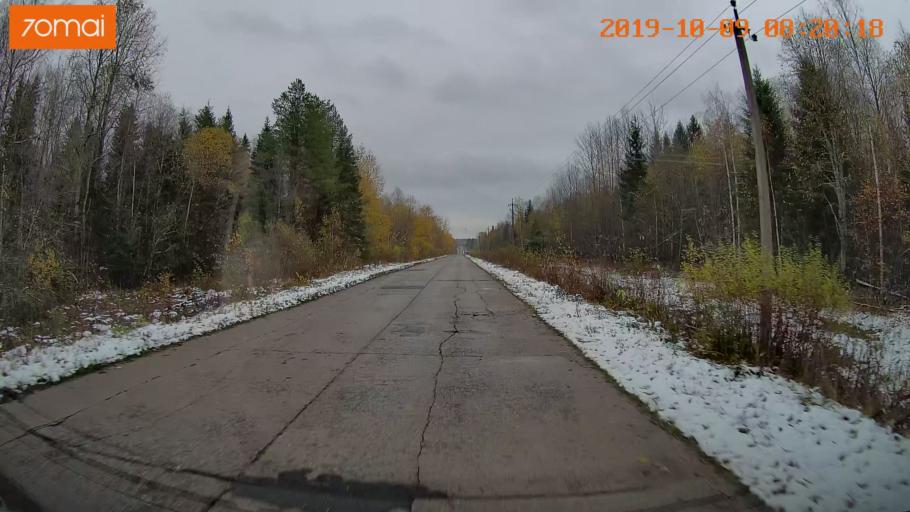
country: RU
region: Vologda
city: Gryazovets
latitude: 58.7428
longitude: 40.2574
